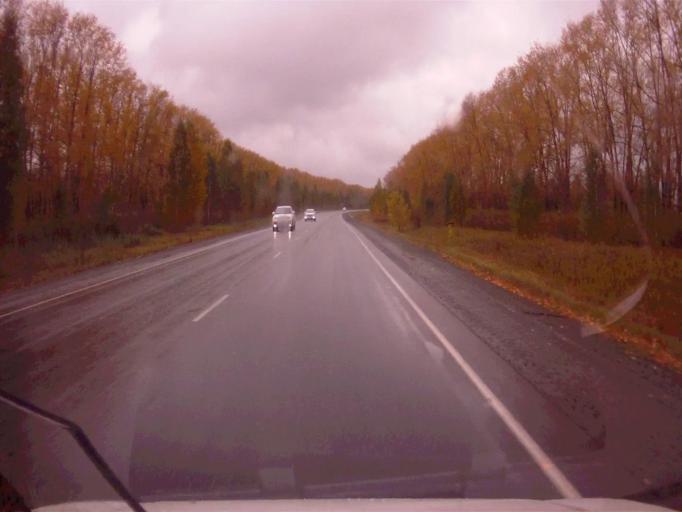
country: RU
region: Chelyabinsk
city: Argayash
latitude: 55.4495
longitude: 60.9403
